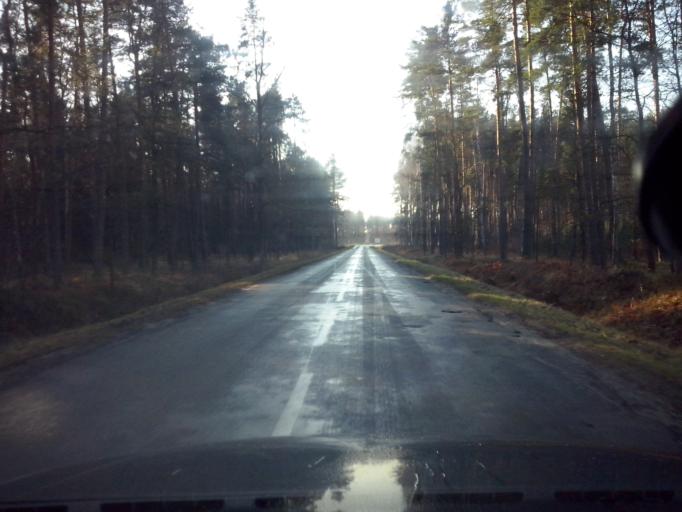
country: PL
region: Subcarpathian Voivodeship
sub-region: Powiat lezajski
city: Letownia
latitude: 50.3669
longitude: 22.2469
